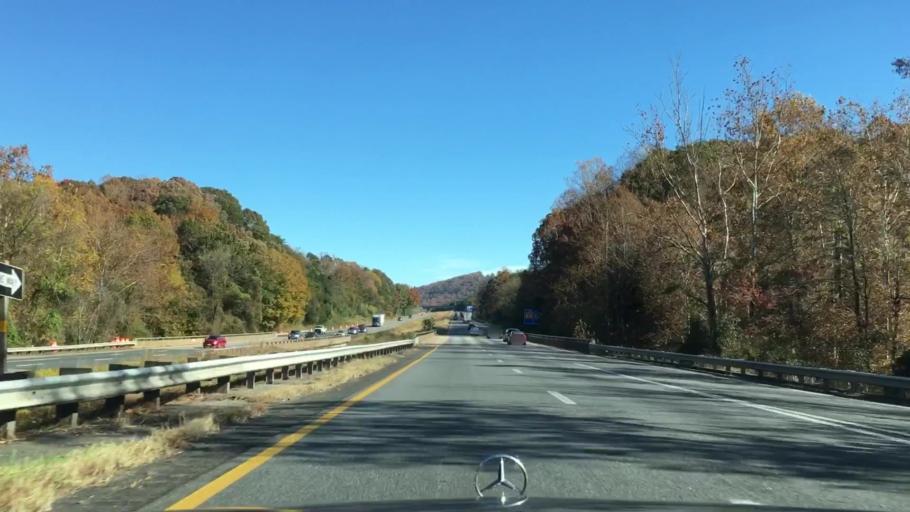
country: US
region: Virginia
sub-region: City of Charlottesville
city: Charlottesville
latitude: 38.0078
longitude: -78.5063
